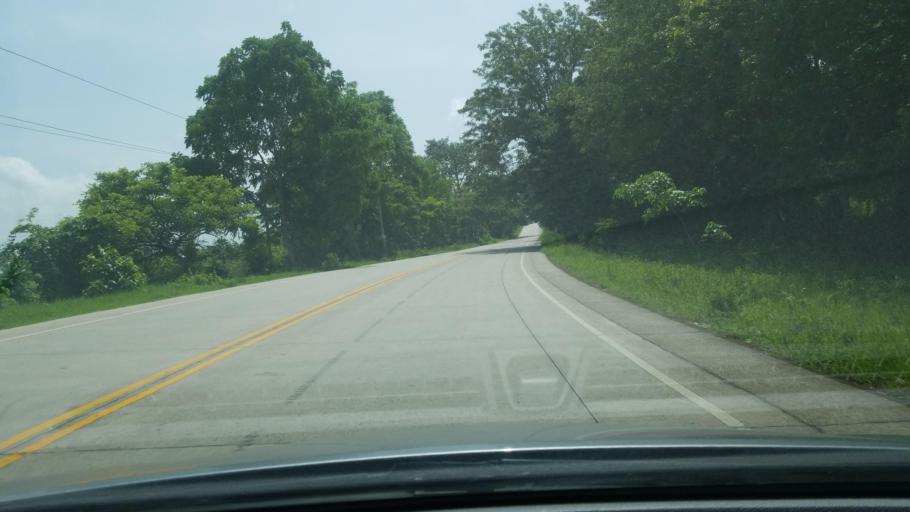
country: HN
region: Copan
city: Florida
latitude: 15.0367
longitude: -88.8240
